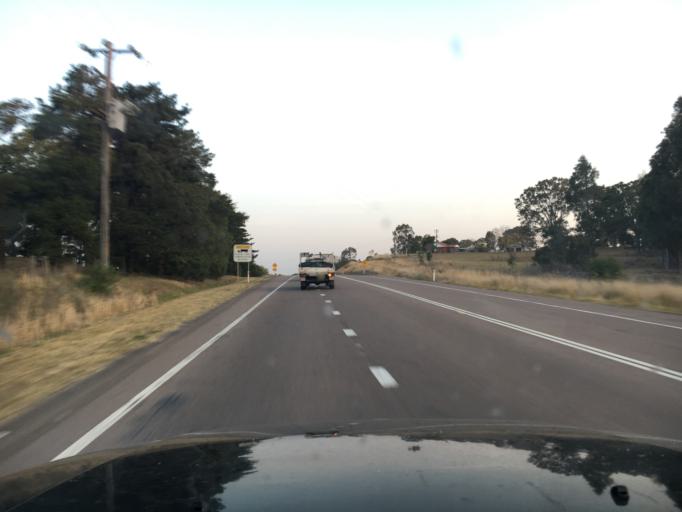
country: AU
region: New South Wales
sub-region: Cessnock
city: Greta
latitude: -32.6904
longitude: 151.4027
